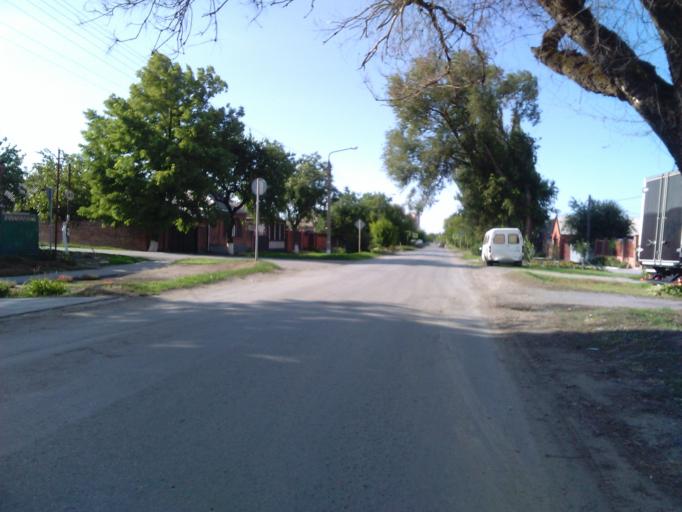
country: RU
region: Rostov
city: Bataysk
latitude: 47.1439
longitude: 39.7356
